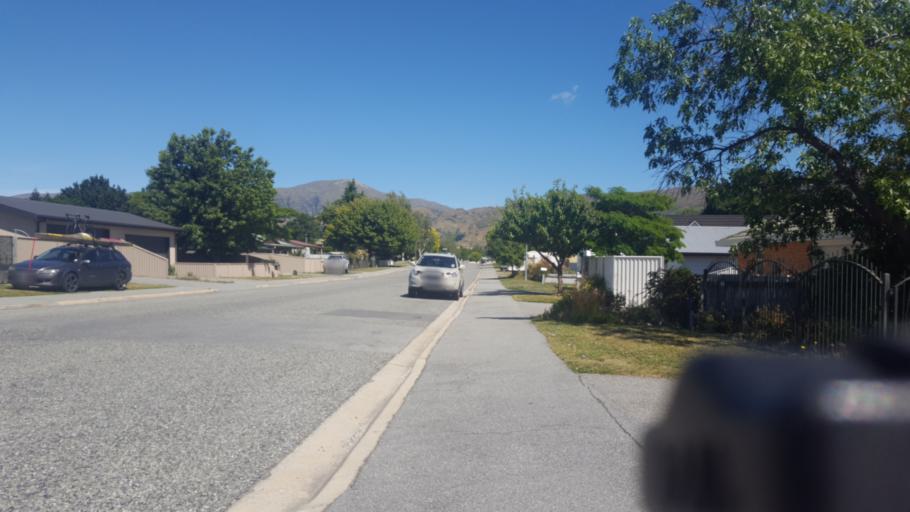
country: NZ
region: Otago
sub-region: Queenstown-Lakes District
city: Wanaka
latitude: -45.0446
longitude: 169.2001
